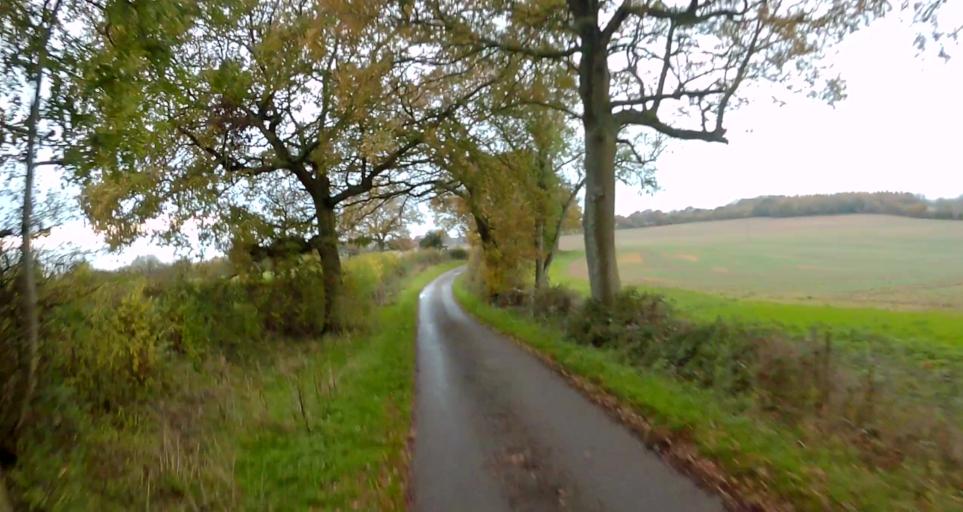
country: GB
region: England
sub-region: Hampshire
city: Long Sutton
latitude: 51.2335
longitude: -0.9062
